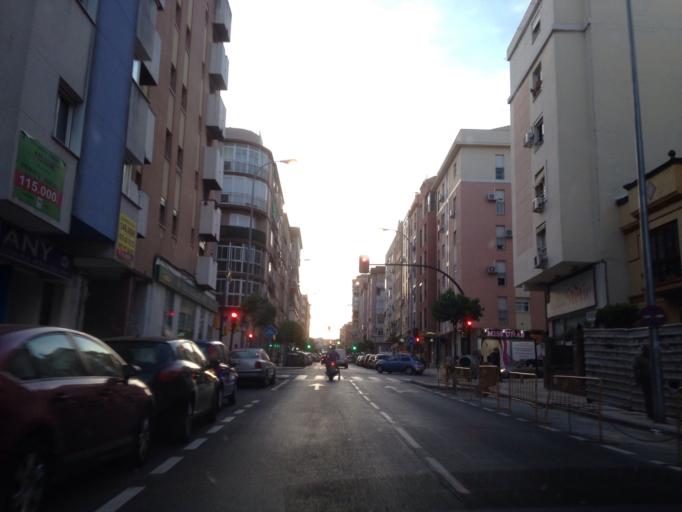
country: ES
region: Andalusia
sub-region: Provincia de Malaga
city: Malaga
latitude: 36.7280
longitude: -4.4403
